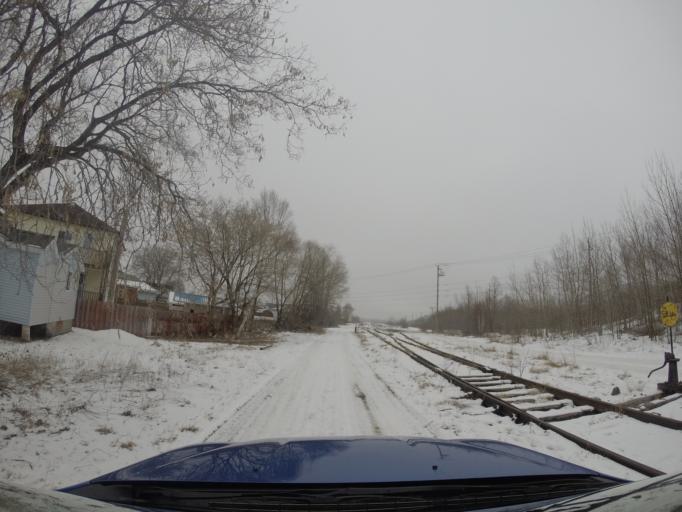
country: CA
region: Ontario
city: Greater Sudbury
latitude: 46.5033
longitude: -80.9814
